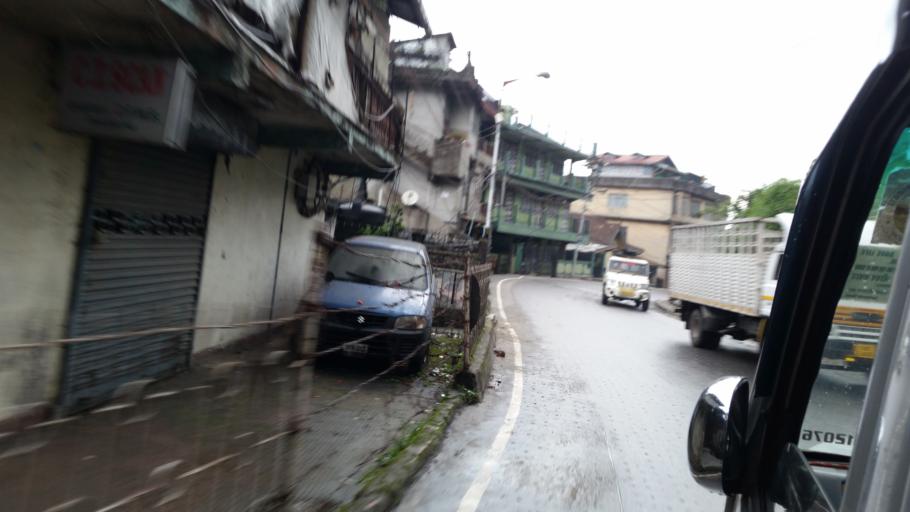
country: IN
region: West Bengal
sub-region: Darjiling
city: Darjiling
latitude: 27.0325
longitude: 88.2576
